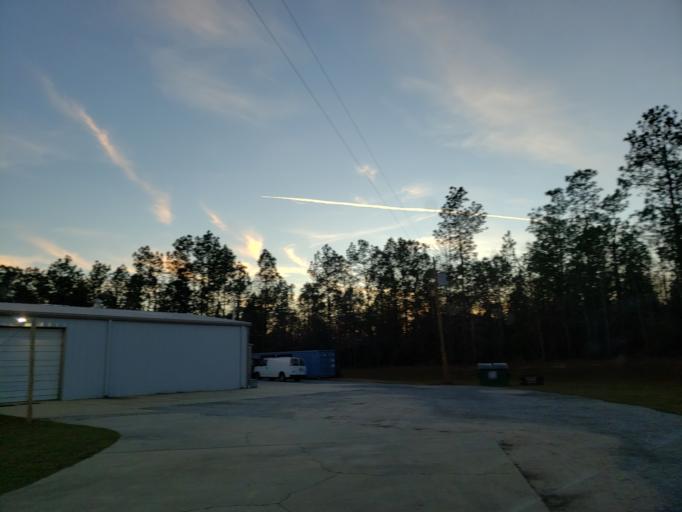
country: US
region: Mississippi
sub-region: Lamar County
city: West Hattiesburg
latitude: 31.2494
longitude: -89.3334
